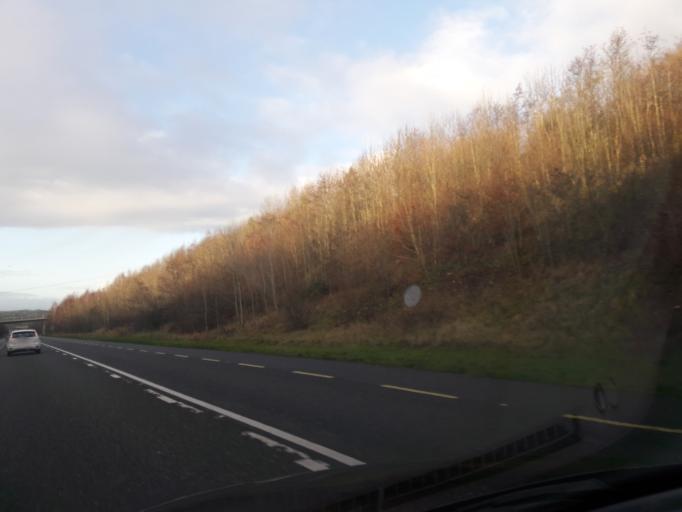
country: IE
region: Ulster
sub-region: County Monaghan
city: Carrickmacross
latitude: 53.9766
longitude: -6.7039
